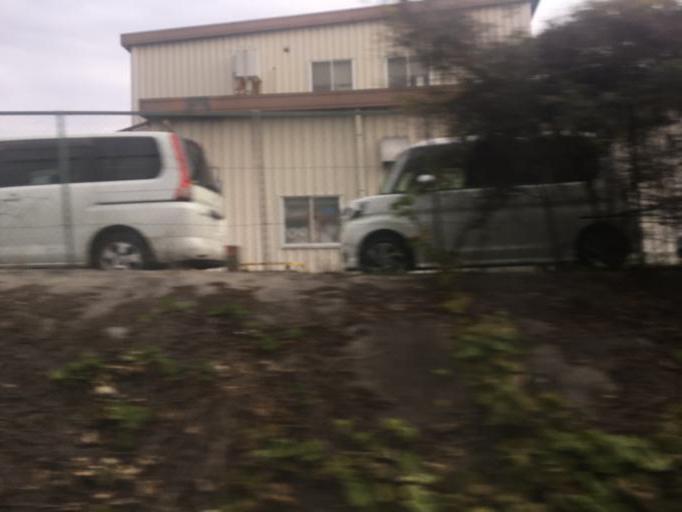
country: JP
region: Saitama
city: Hanno
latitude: 35.7987
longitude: 139.3348
